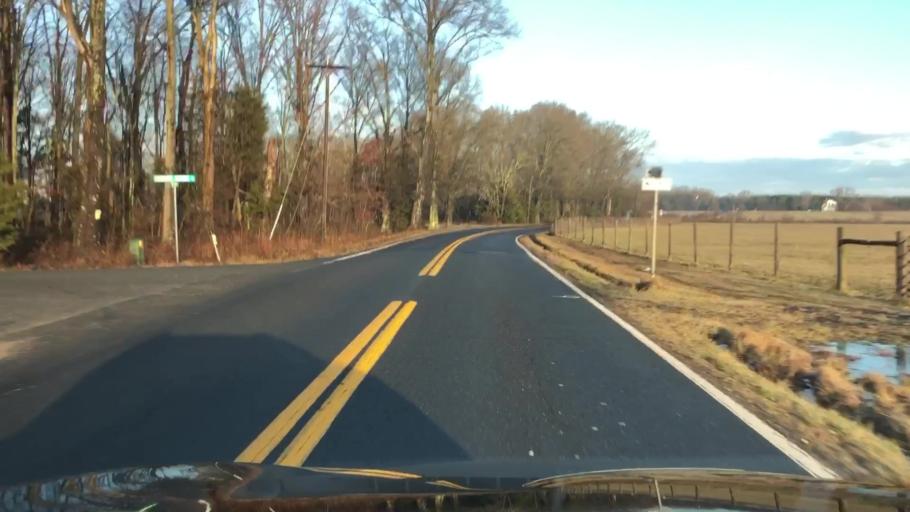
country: US
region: Virginia
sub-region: Fauquier County
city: Bealeton
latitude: 38.5809
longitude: -77.6961
